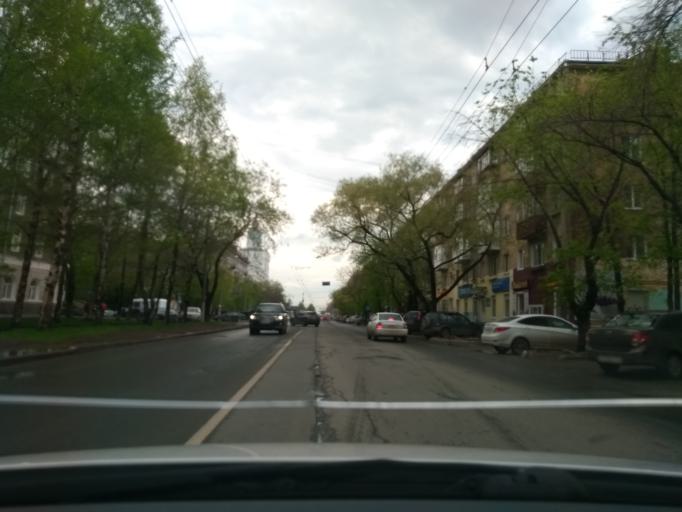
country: RU
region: Perm
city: Perm
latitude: 57.9933
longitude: 56.2561
